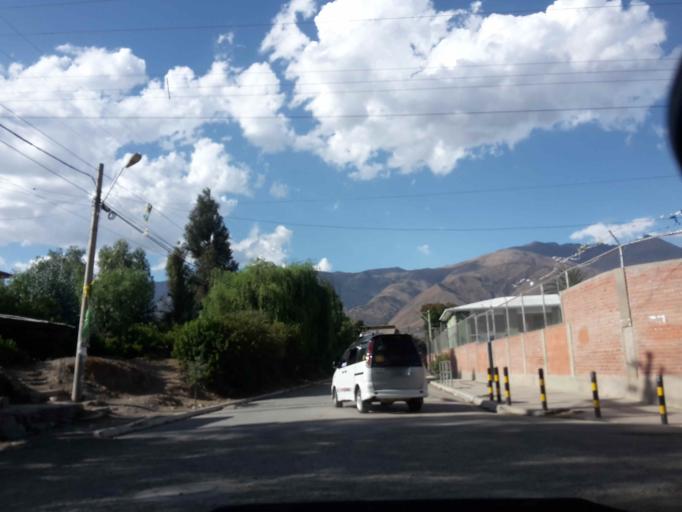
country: BO
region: Cochabamba
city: Cochabamba
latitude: -17.3628
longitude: -66.2077
